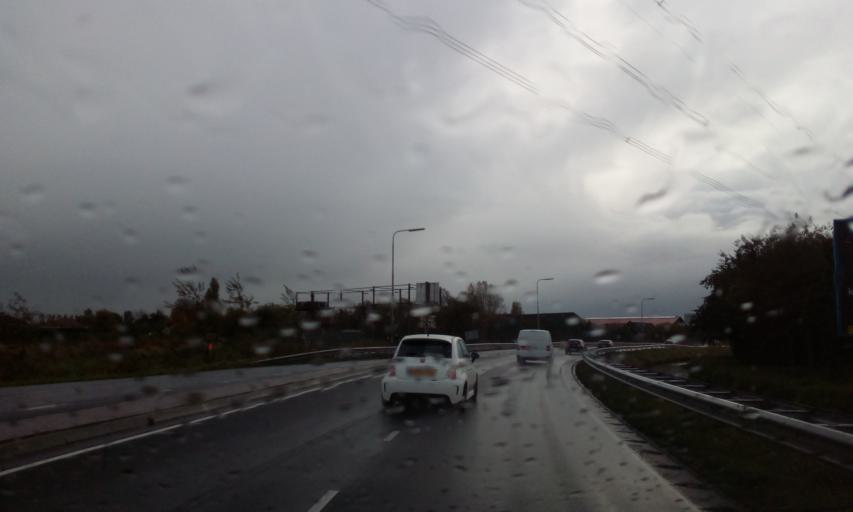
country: NL
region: South Holland
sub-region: Gemeente Westland
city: Kwintsheul
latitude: 52.0091
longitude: 4.2894
